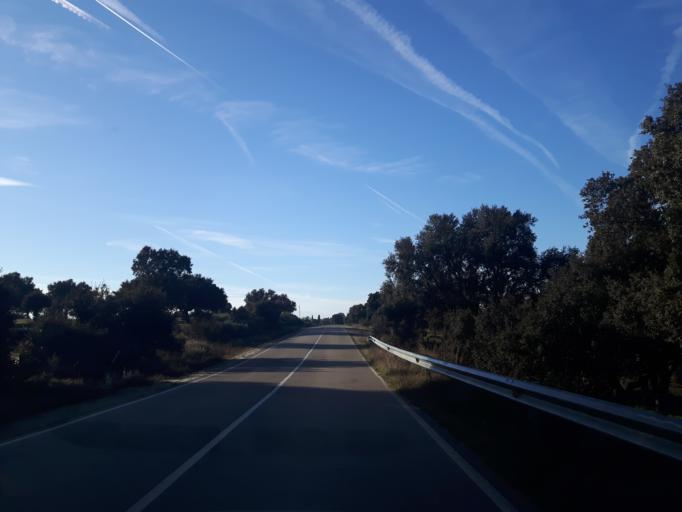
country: ES
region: Castille and Leon
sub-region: Provincia de Salamanca
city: Olmedo de Camaces
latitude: 40.8875
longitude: -6.6240
